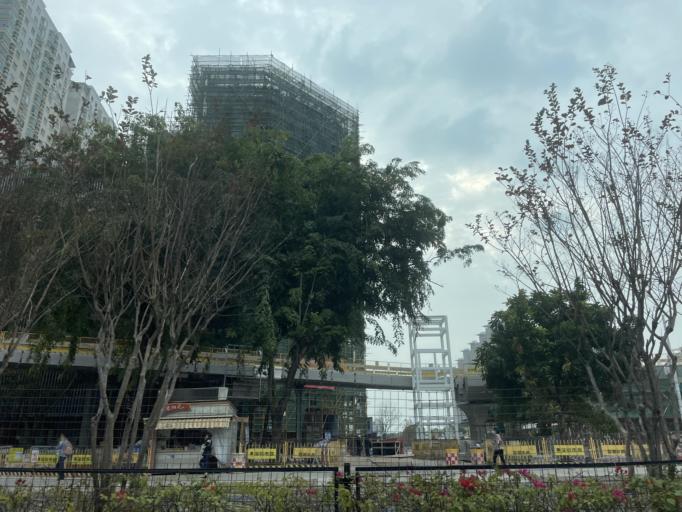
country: CN
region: Guangdong
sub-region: Shenzhen
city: Shenzhen
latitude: 22.5208
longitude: 114.0425
